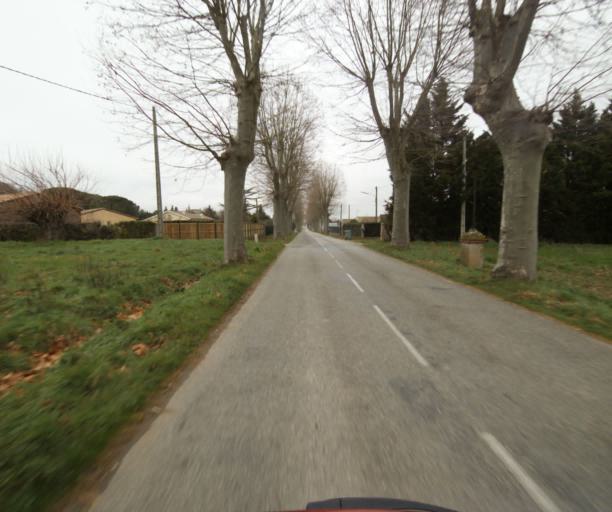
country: FR
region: Midi-Pyrenees
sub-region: Departement de la Haute-Garonne
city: Gaillac-Toulza
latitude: 43.2717
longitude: 1.5087
